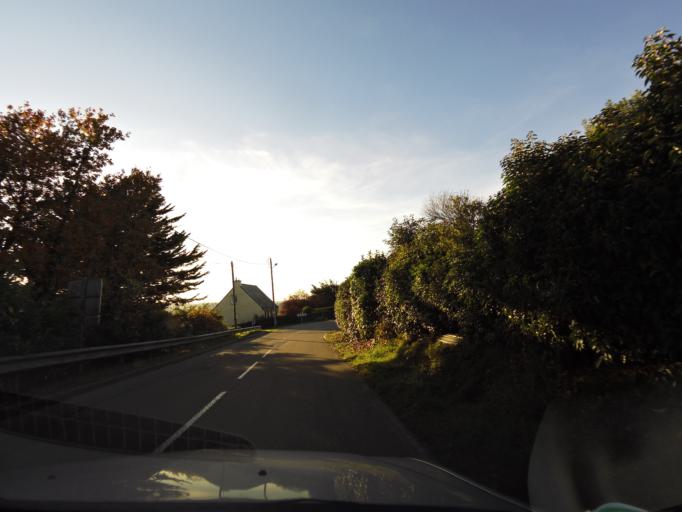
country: FR
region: Brittany
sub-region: Departement d'Ille-et-Vilaine
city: Pance
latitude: 47.8861
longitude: -1.6831
